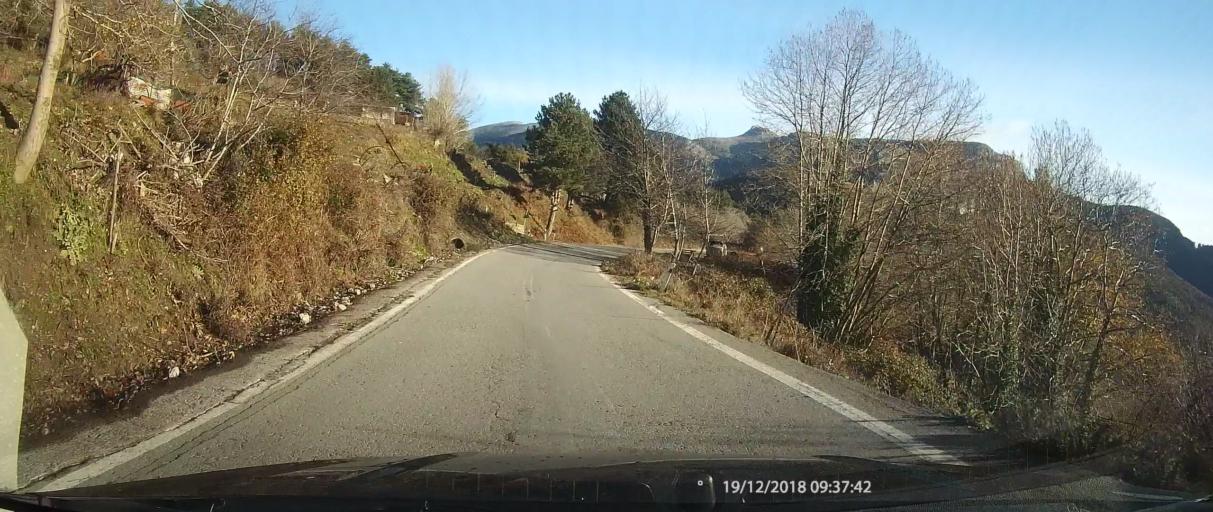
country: GR
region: Peloponnese
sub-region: Nomos Lakonias
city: Magoula
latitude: 37.0811
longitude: 22.2783
